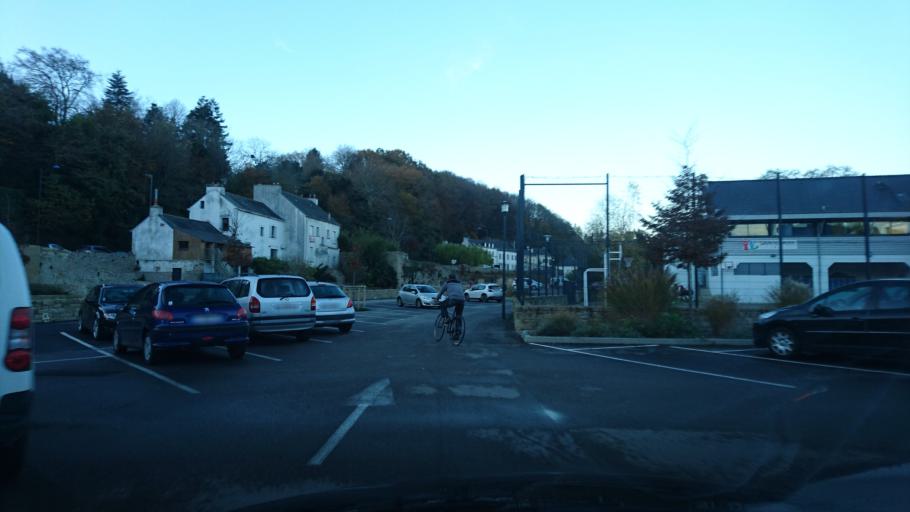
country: FR
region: Brittany
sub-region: Departement du Finistere
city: Quimperle
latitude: 47.8734
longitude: -3.5466
